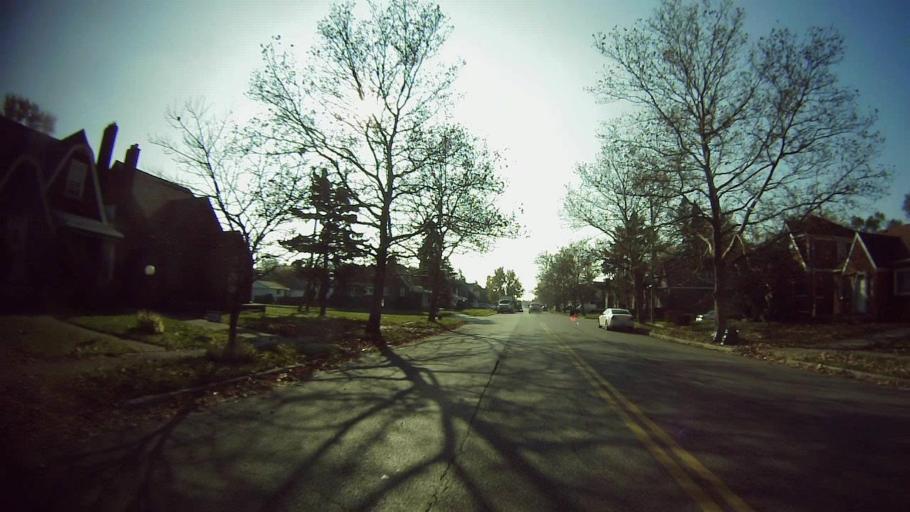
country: US
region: Michigan
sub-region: Wayne County
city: Dearborn
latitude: 42.3600
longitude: -83.1677
